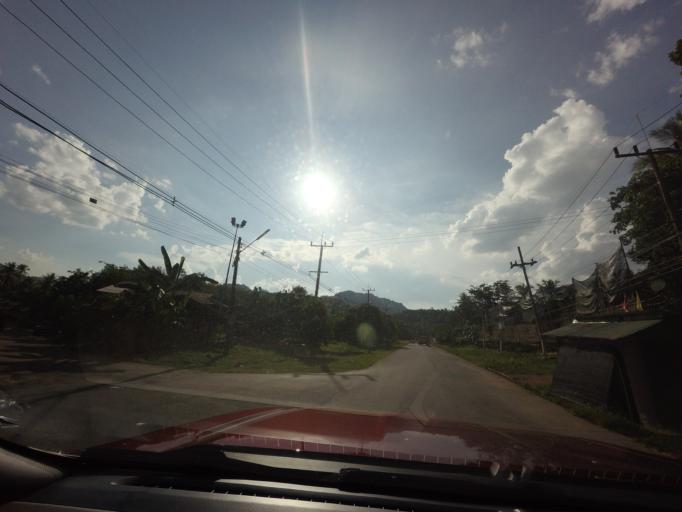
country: TH
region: Yala
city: Than To
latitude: 6.1963
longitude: 101.2424
